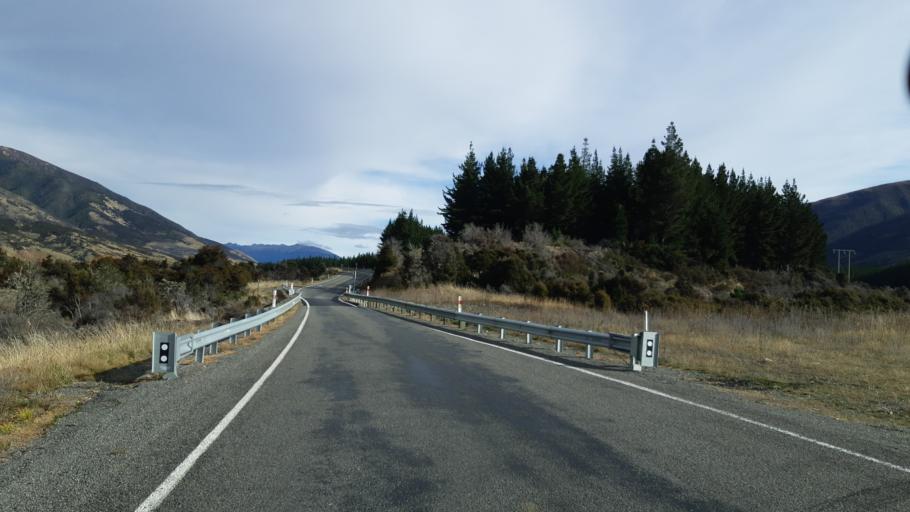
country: NZ
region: Tasman
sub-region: Tasman District
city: Wakefield
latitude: -41.7155
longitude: 173.0814
